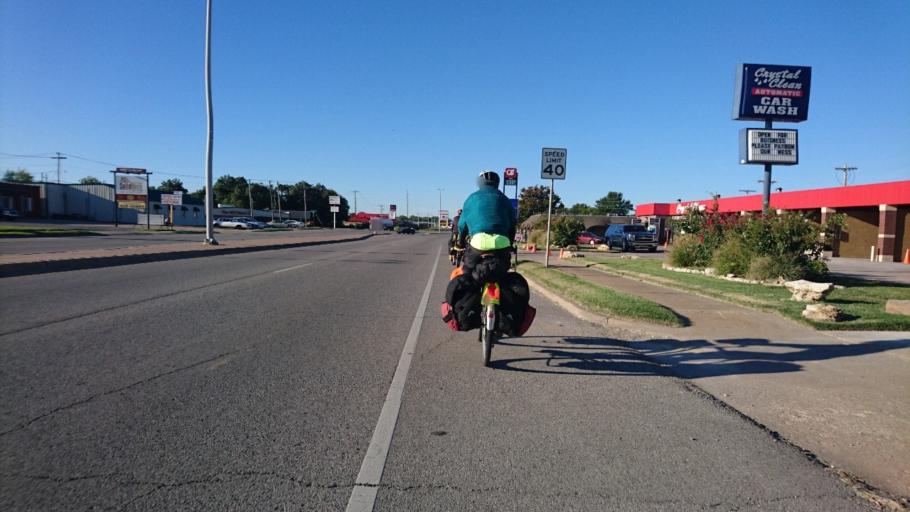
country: US
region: Oklahoma
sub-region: Rogers County
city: Claremore
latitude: 36.3094
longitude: -95.6182
